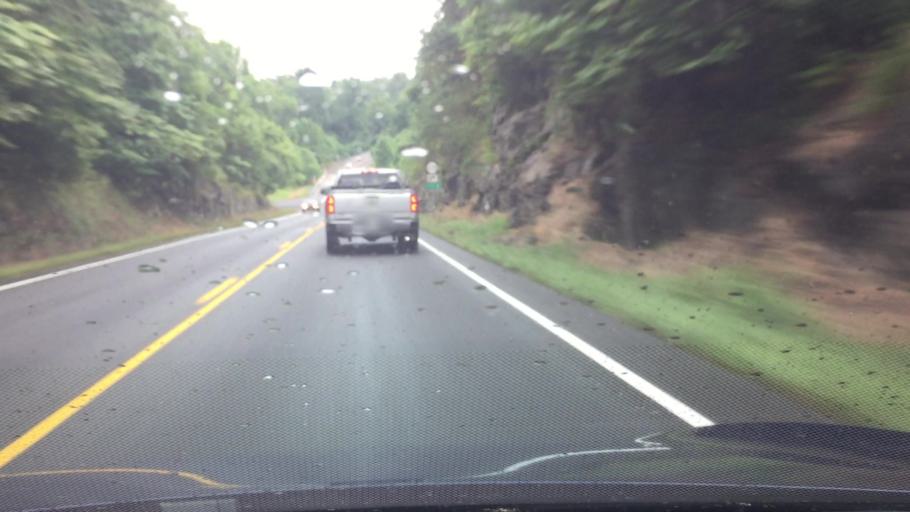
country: US
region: Virginia
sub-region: City of Bedford
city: Bedford
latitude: 37.3656
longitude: -79.4168
